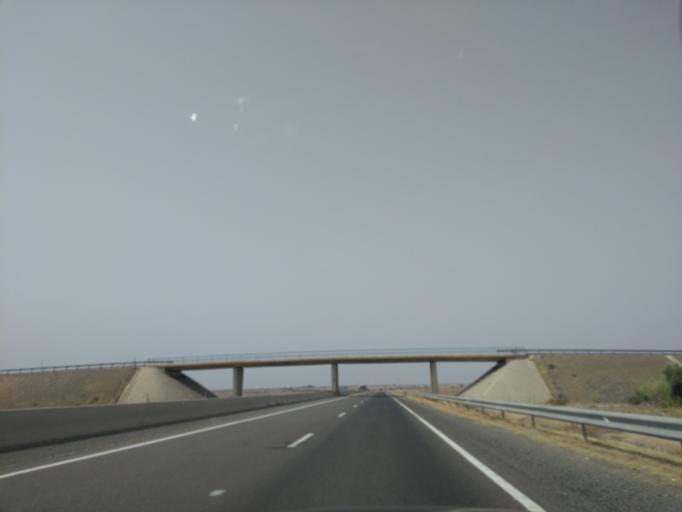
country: MA
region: Marrakech-Tensift-Al Haouz
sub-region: Marrakech
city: Marrakesh
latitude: 31.7418
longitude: -8.2117
